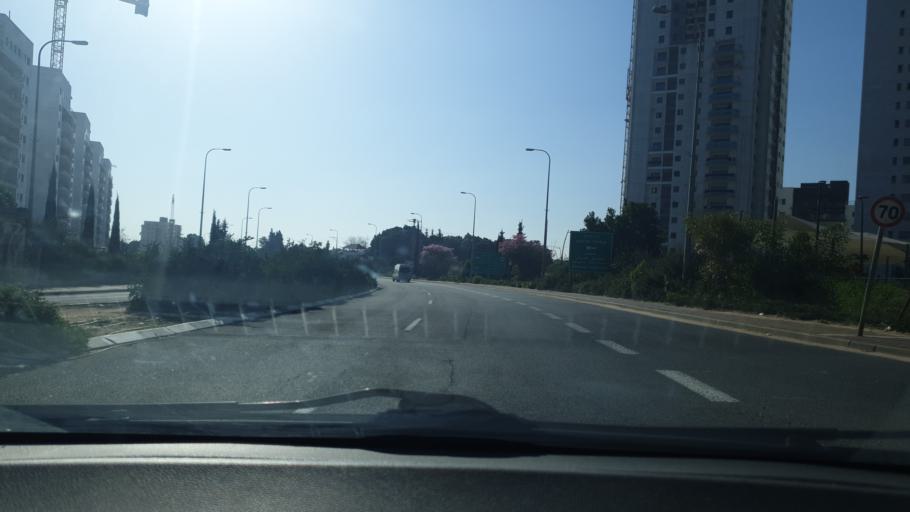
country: IL
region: Central District
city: Ness Ziona
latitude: 31.9465
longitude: 34.8319
